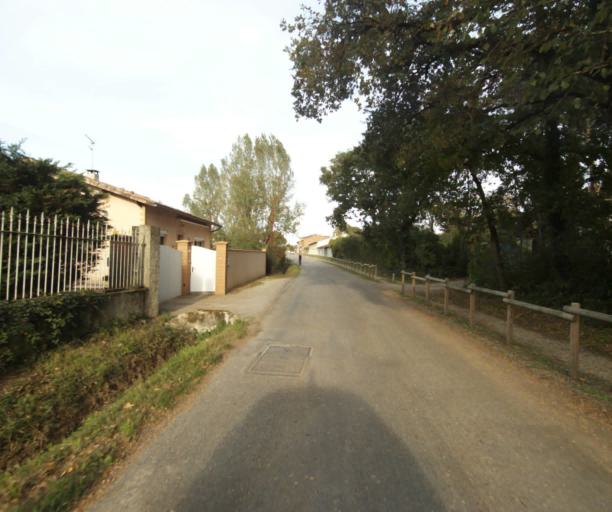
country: FR
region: Midi-Pyrenees
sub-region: Departement du Tarn-et-Garonne
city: Campsas
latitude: 43.8957
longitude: 1.3242
